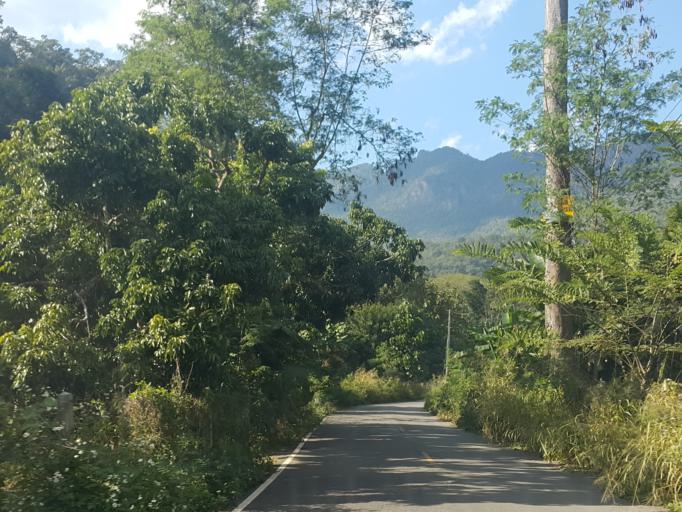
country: TH
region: Chiang Mai
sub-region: Amphoe Chiang Dao
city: Chiang Dao
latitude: 19.4074
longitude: 98.9245
